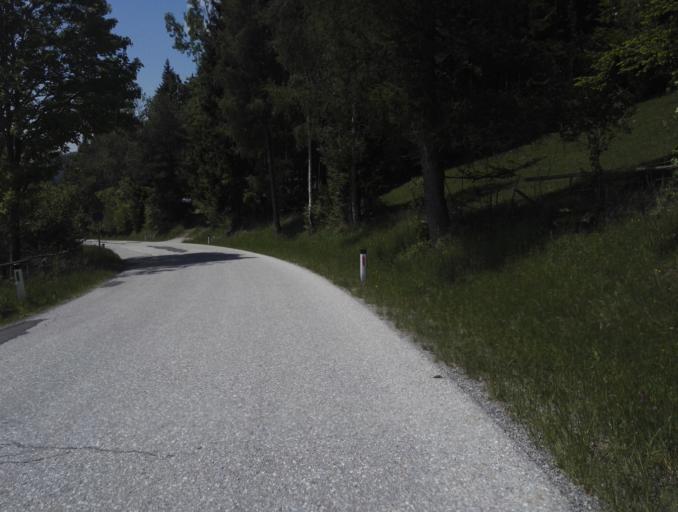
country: AT
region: Styria
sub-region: Politischer Bezirk Graz-Umgebung
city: Sankt Radegund bei Graz
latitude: 47.1963
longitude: 15.4849
